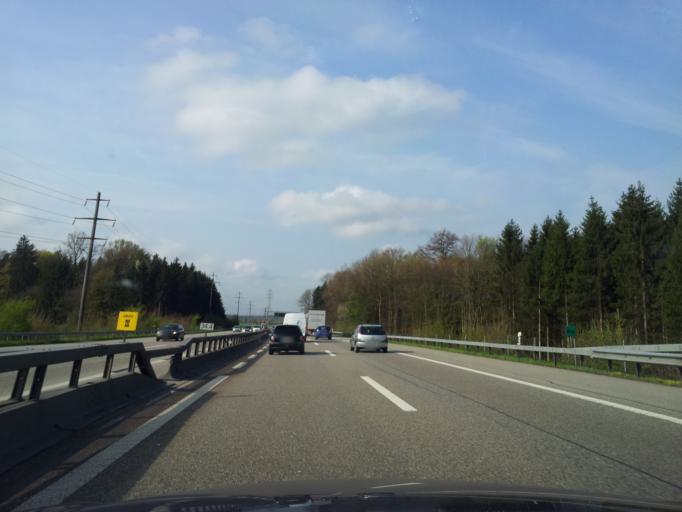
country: CH
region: Bern
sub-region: Oberaargau
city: Wiedlisbach
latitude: 47.2349
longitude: 7.6328
